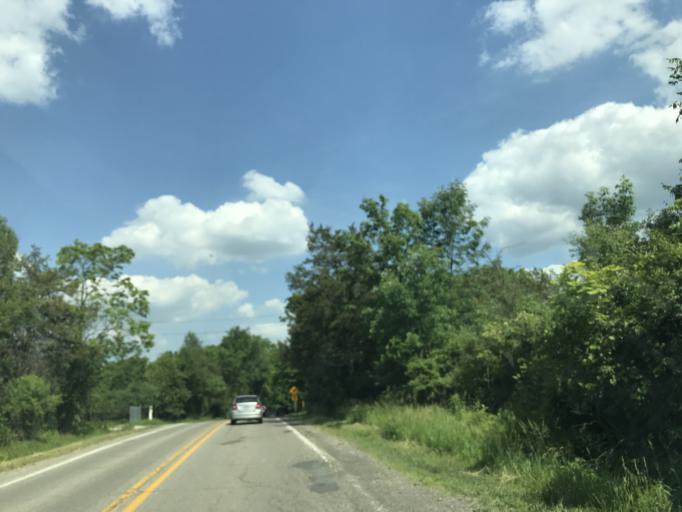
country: US
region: Michigan
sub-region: Washtenaw County
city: Ypsilanti
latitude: 42.2786
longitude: -83.6416
